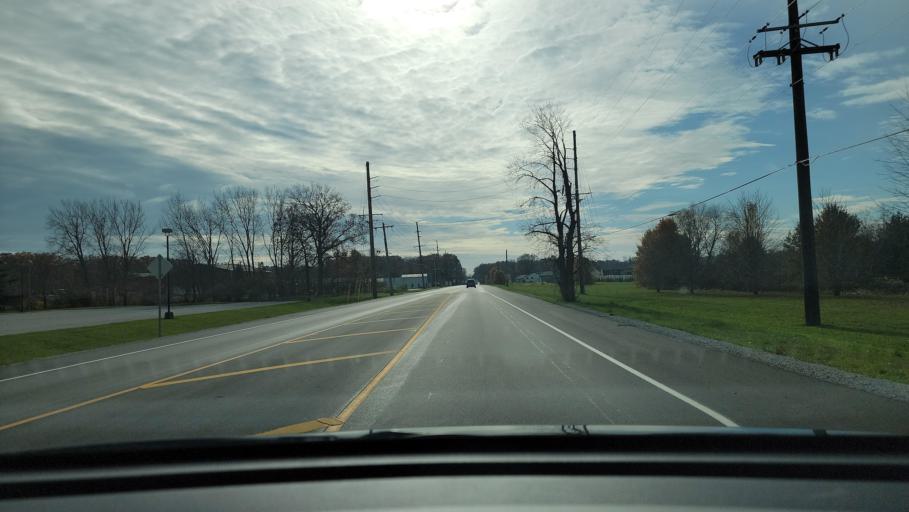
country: US
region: Indiana
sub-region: Porter County
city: Burns Harbor
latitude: 41.5857
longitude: -87.1246
